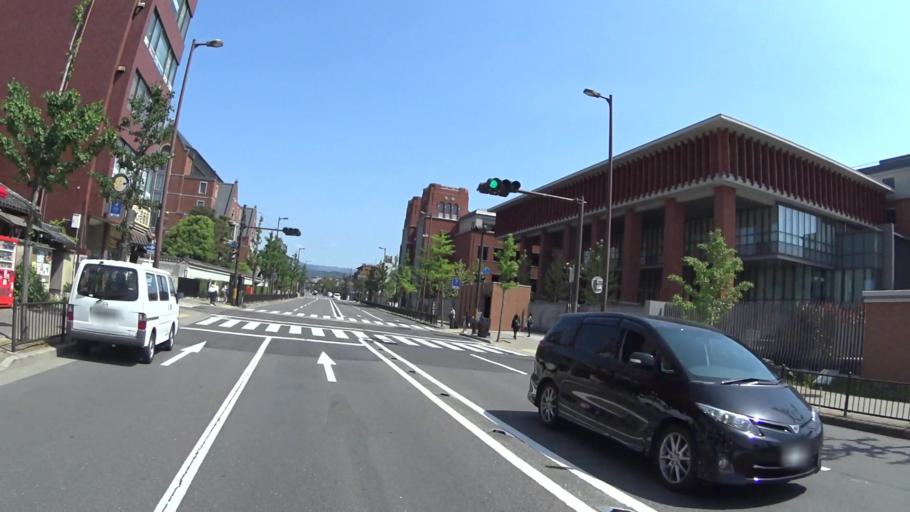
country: JP
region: Kyoto
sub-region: Kyoto-shi
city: Kamigyo-ku
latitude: 35.0301
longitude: 135.7593
